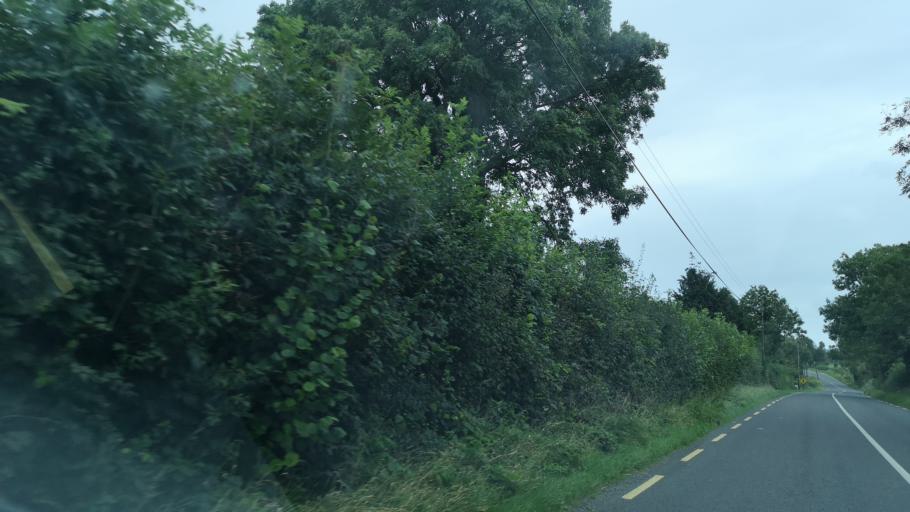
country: IE
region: Leinster
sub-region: Uibh Fhaili
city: Ferbane
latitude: 53.2248
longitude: -7.8514
